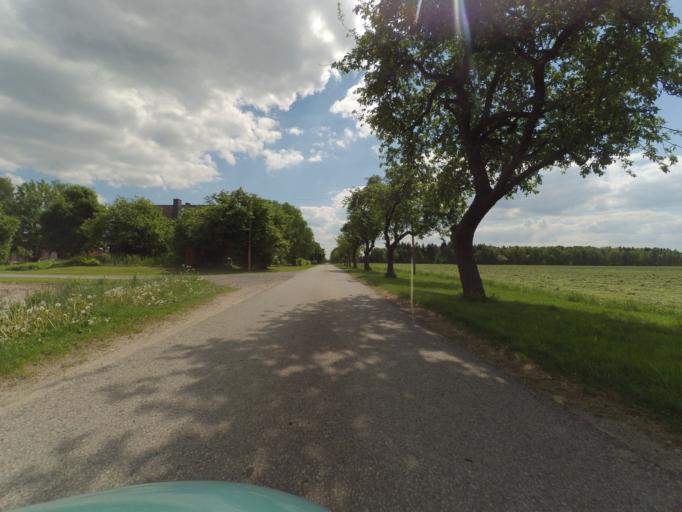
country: DE
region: Lower Saxony
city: Steinhorst
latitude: 52.6478
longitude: 10.3829
